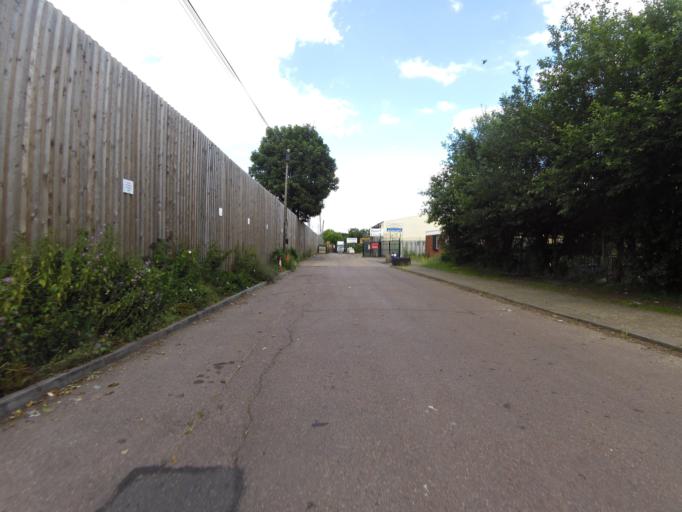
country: GB
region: England
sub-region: Suffolk
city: Kesgrave
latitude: 52.0369
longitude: 1.1997
